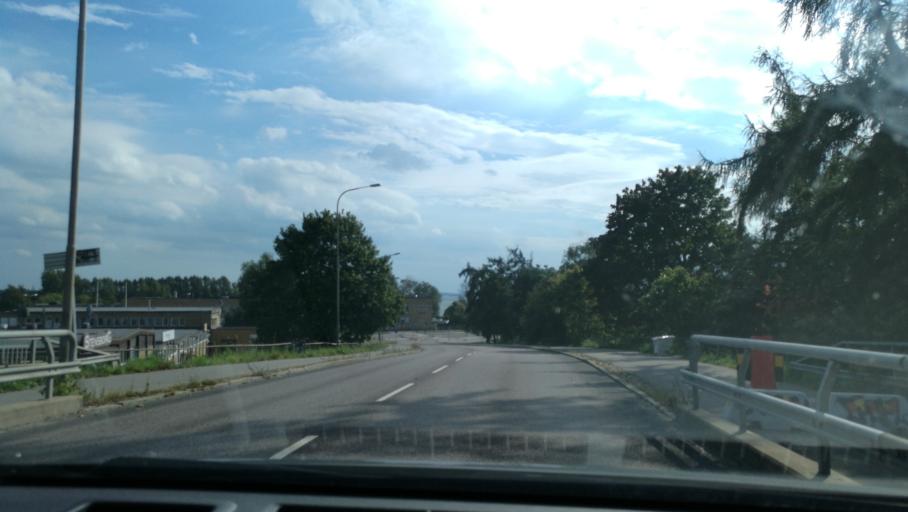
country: SE
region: Vaestmanland
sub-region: Vasteras
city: Vasteras
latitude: 59.5979
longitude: 16.5244
